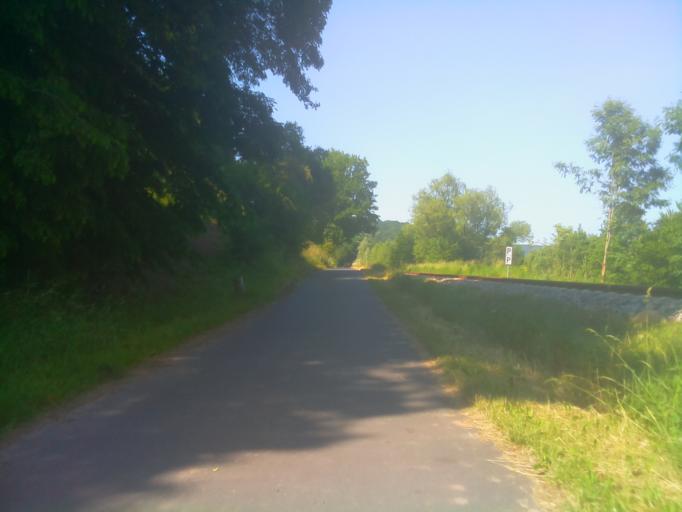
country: DE
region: Thuringia
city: Freienorla
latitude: 50.7657
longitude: 11.5380
